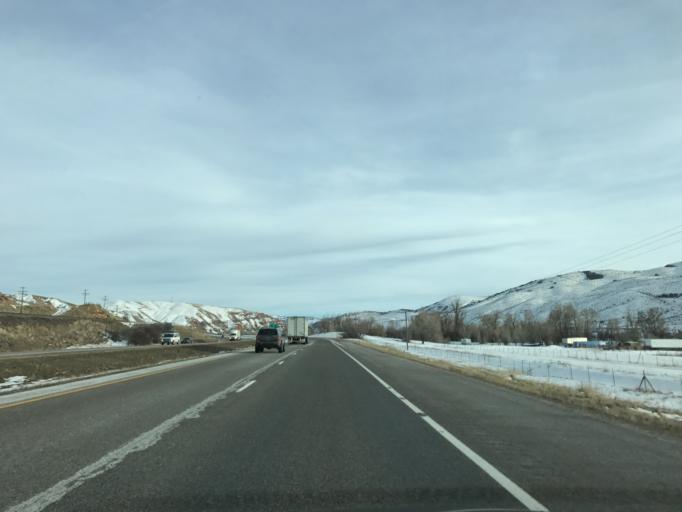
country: US
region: Utah
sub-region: Summit County
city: Coalville
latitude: 40.9972
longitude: -111.4655
